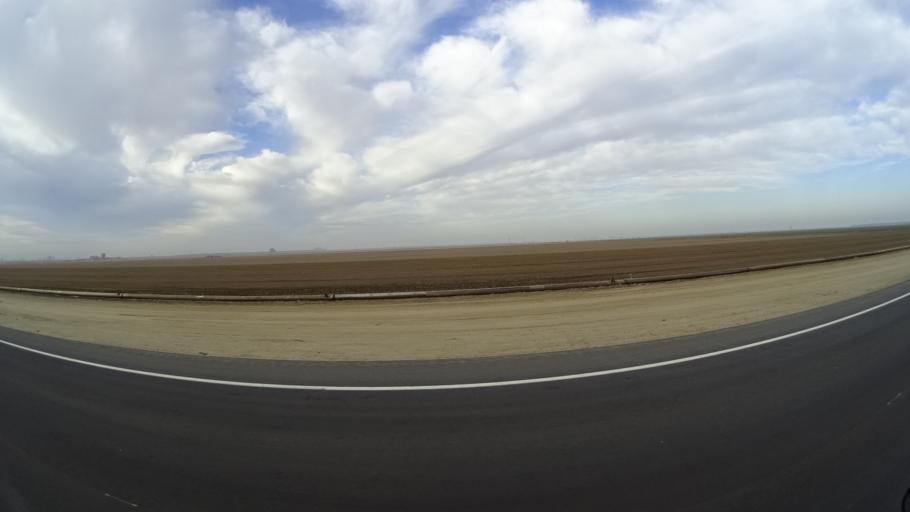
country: US
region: California
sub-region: Kern County
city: Rosedale
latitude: 35.4037
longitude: -119.1987
